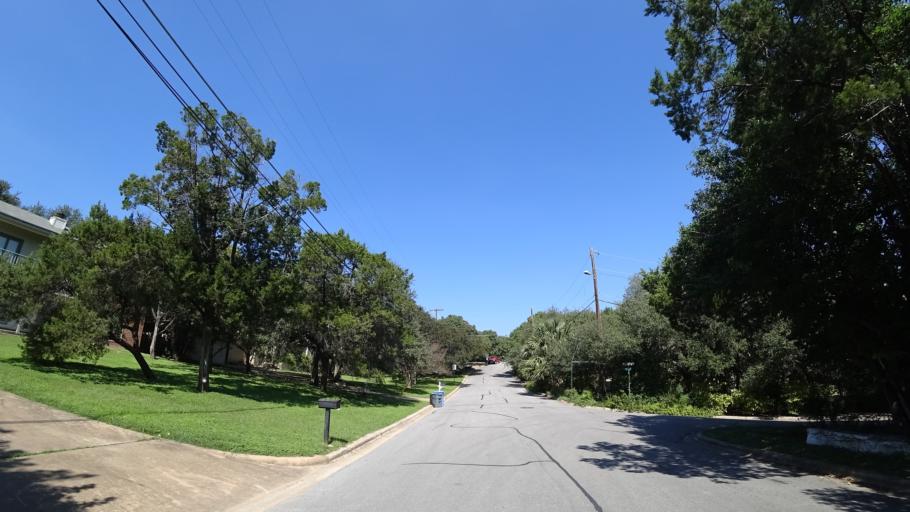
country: US
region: Texas
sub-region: Travis County
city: Rollingwood
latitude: 30.2796
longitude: -97.7850
